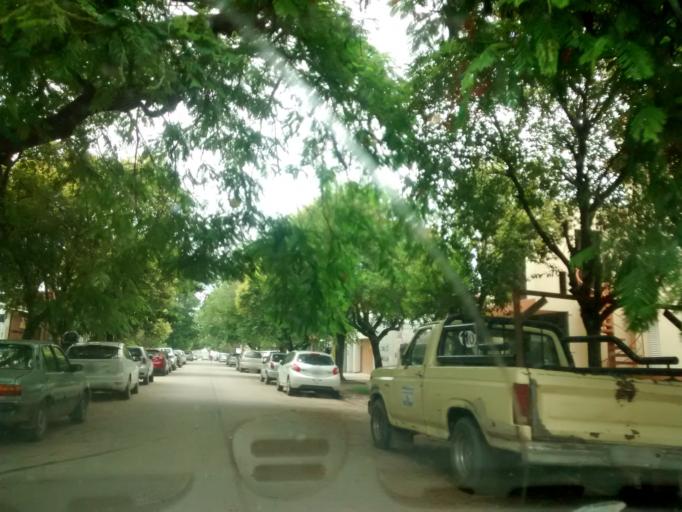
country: AR
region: Chaco
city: Resistencia
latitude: -27.4544
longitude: -58.9793
